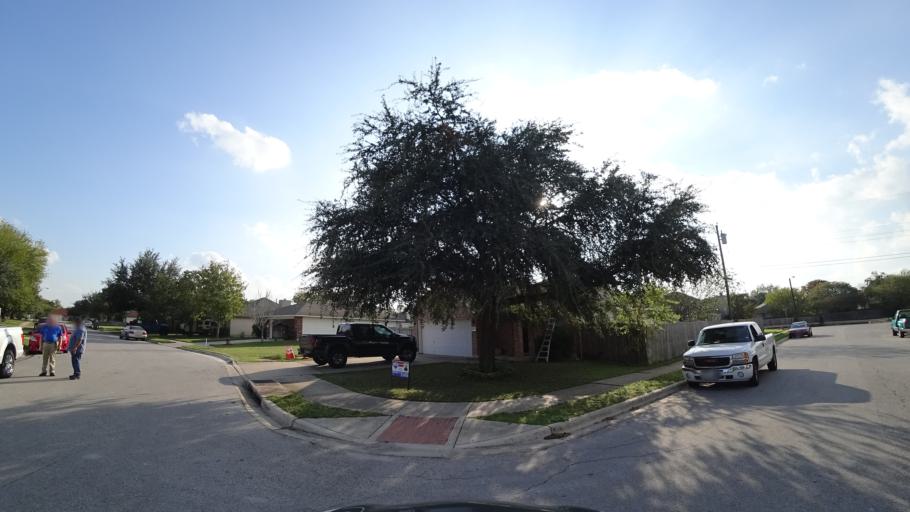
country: US
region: Texas
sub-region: Williamson County
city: Round Rock
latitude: 30.4958
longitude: -97.6611
